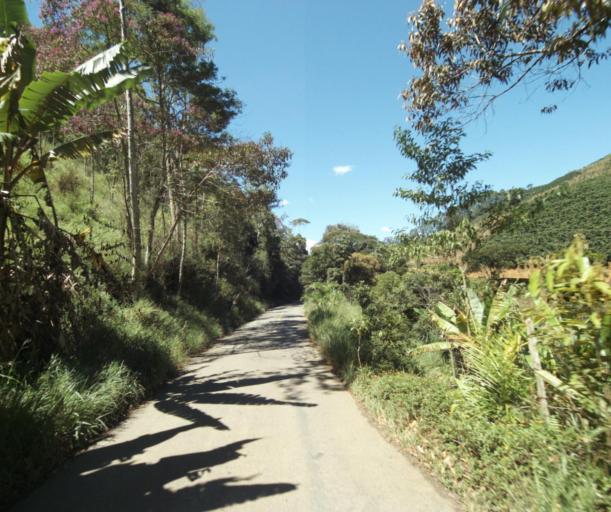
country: BR
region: Minas Gerais
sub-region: Espera Feliz
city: Espera Feliz
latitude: -20.6380
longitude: -41.8185
